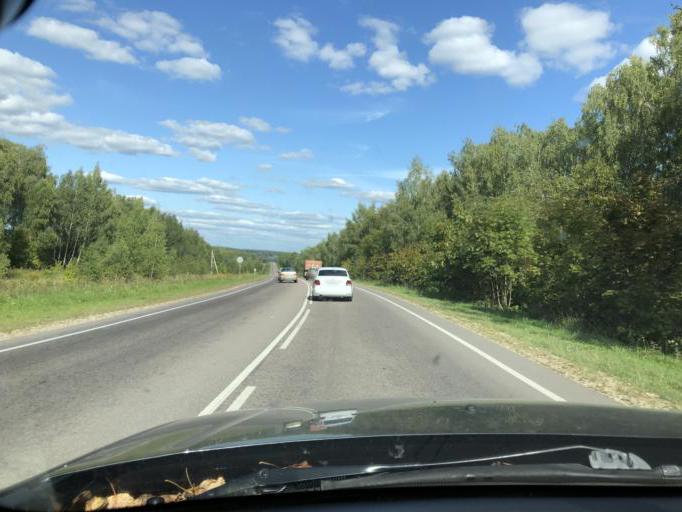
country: RU
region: Tula
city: Pervomayskiy
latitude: 54.1332
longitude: 37.3632
